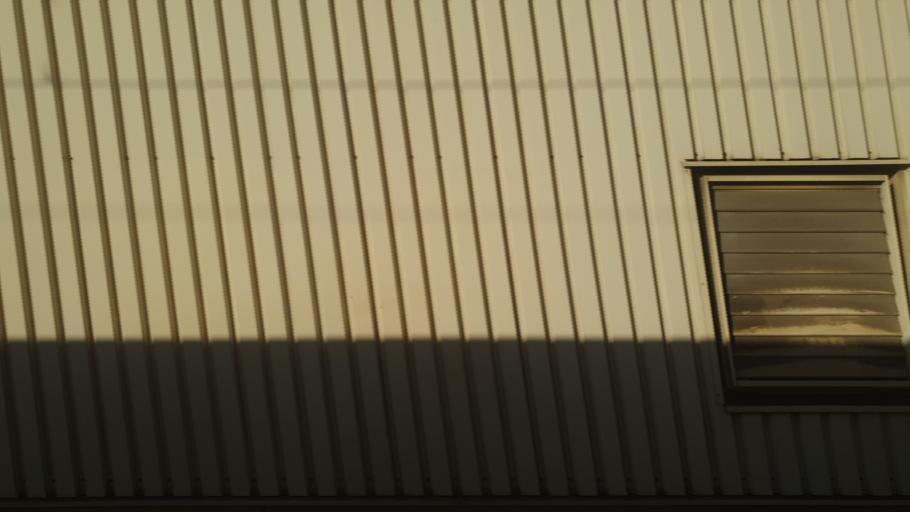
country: DE
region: Bavaria
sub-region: Regierungsbezirk Unterfranken
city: Iphofen
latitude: 49.6980
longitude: 10.2525
